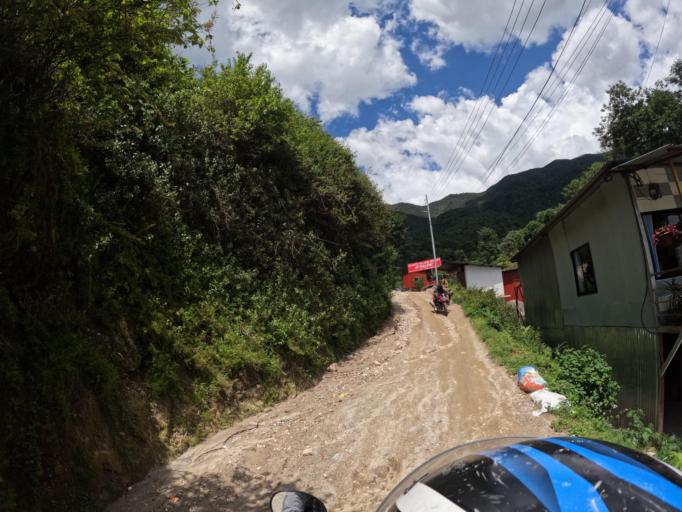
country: NP
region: Central Region
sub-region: Bagmati Zone
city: Kathmandu
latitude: 27.8008
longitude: 85.3299
